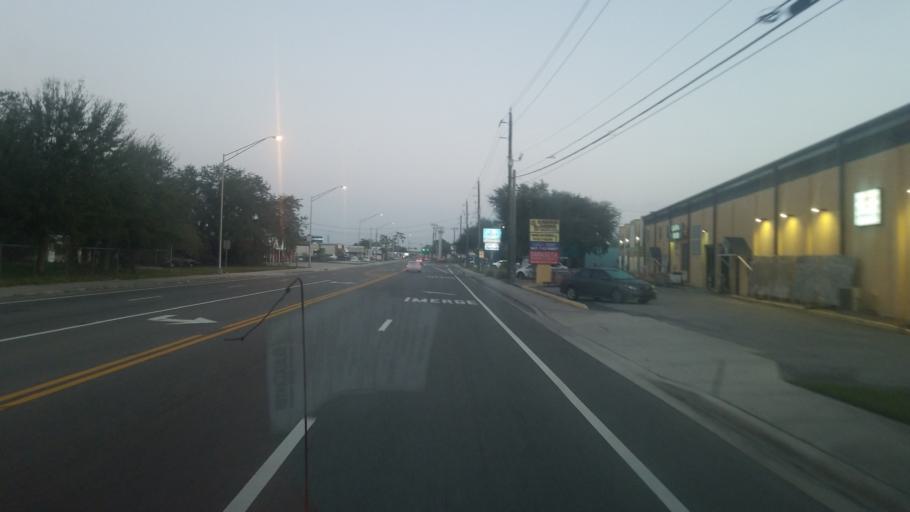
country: US
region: Florida
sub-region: Sarasota County
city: Fruitville
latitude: 27.3233
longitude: -82.4513
